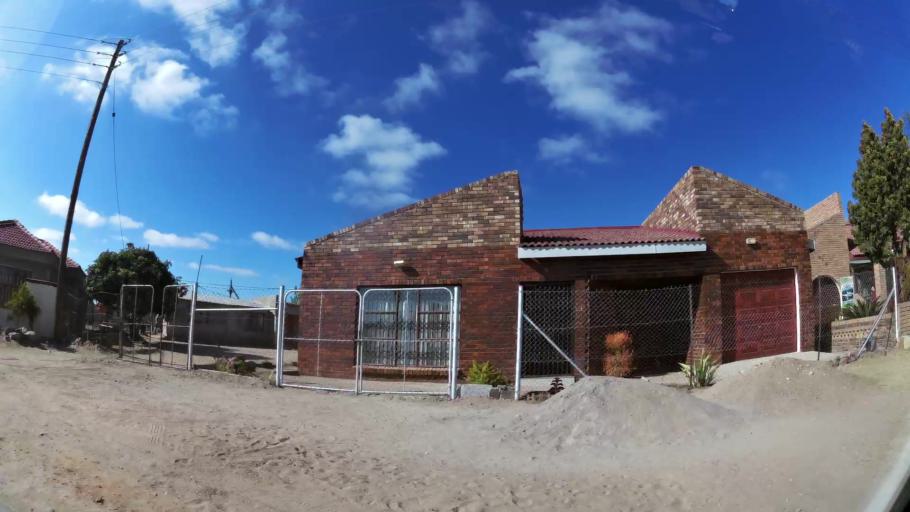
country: ZA
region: Limpopo
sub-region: Capricorn District Municipality
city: Polokwane
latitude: -23.8572
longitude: 29.3650
